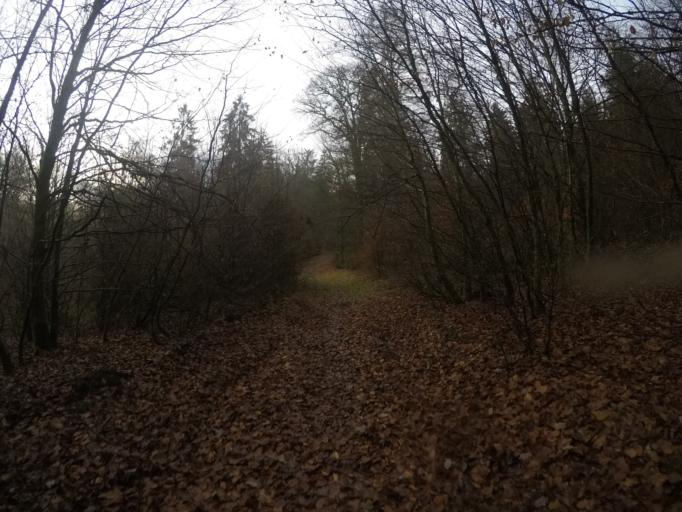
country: BE
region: Wallonia
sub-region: Province du Luxembourg
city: Habay-la-Vieille
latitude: 49.7588
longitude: 5.5993
